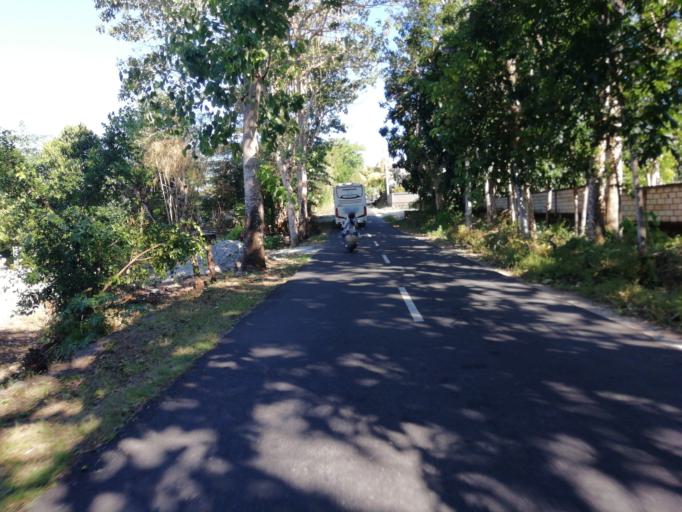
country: ID
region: Bali
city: Jimbaran
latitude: -8.8319
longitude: 115.1773
